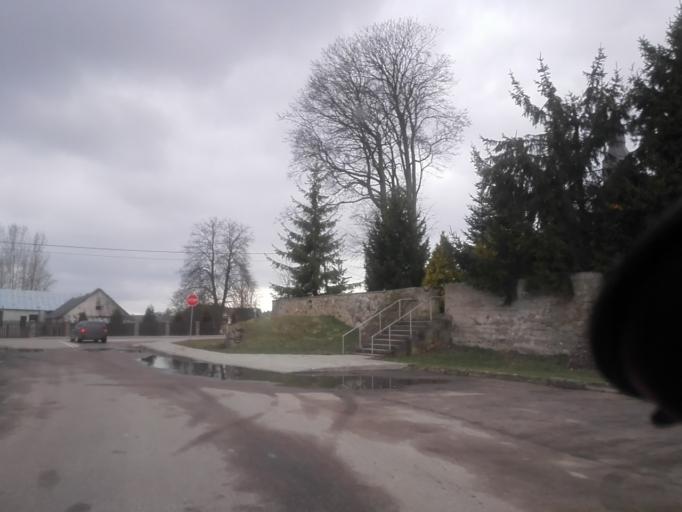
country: PL
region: Podlasie
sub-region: Suwalki
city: Suwalki
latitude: 54.2068
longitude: 22.9133
